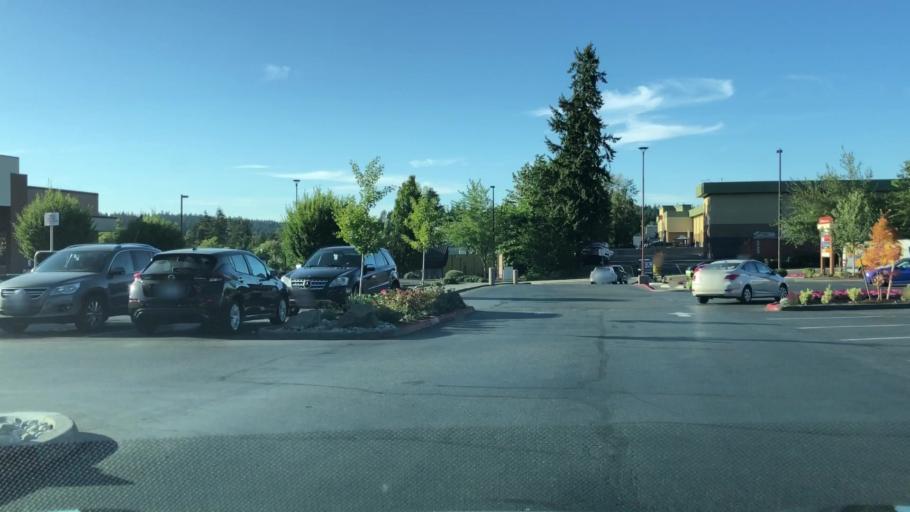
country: US
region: Washington
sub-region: King County
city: Redmond
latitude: 47.6270
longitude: -122.1458
